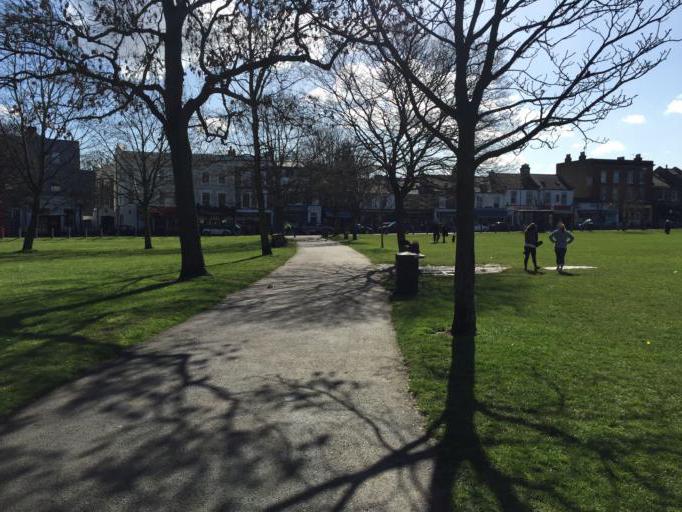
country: GB
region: England
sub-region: Greater London
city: Earlsfield
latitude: 51.4464
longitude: -0.1666
